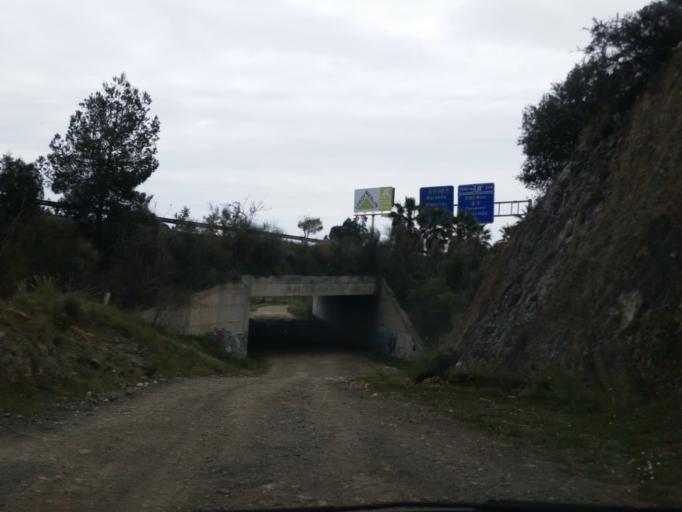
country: ES
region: Andalusia
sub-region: Provincia de Malaga
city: Mijas
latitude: 36.5810
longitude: -4.6082
